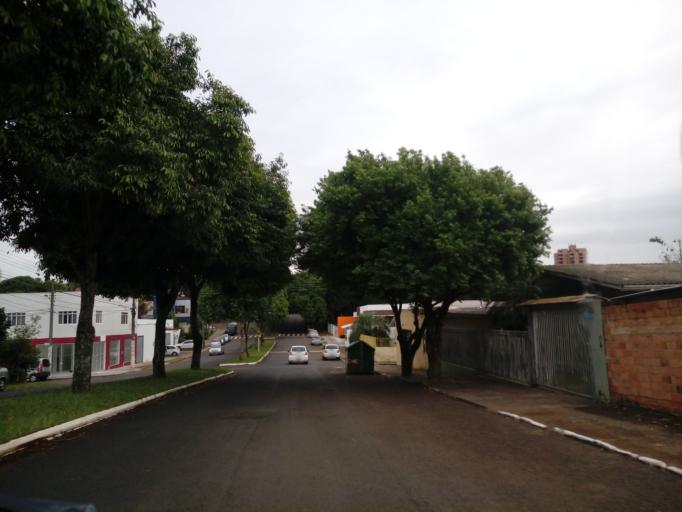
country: BR
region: Santa Catarina
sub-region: Chapeco
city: Chapeco
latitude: -27.0969
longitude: -52.6068
